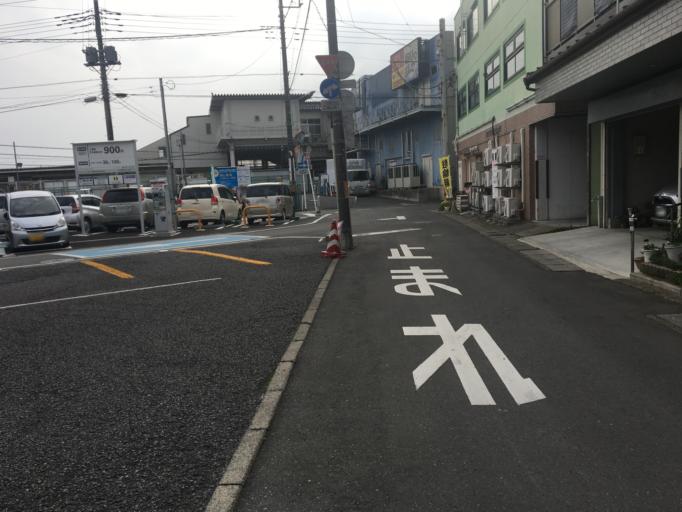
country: JP
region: Saitama
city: Sugito
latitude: 36.0253
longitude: 139.7276
